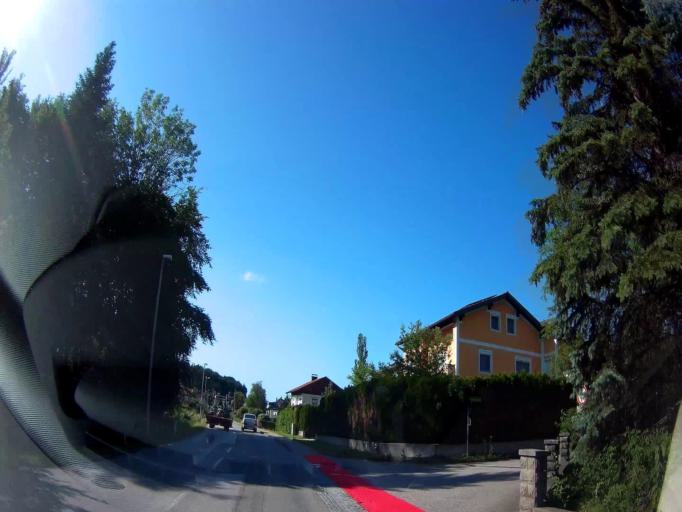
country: AT
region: Salzburg
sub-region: Politischer Bezirk Salzburg-Umgebung
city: Dorfbeuern
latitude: 48.0483
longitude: 12.9878
